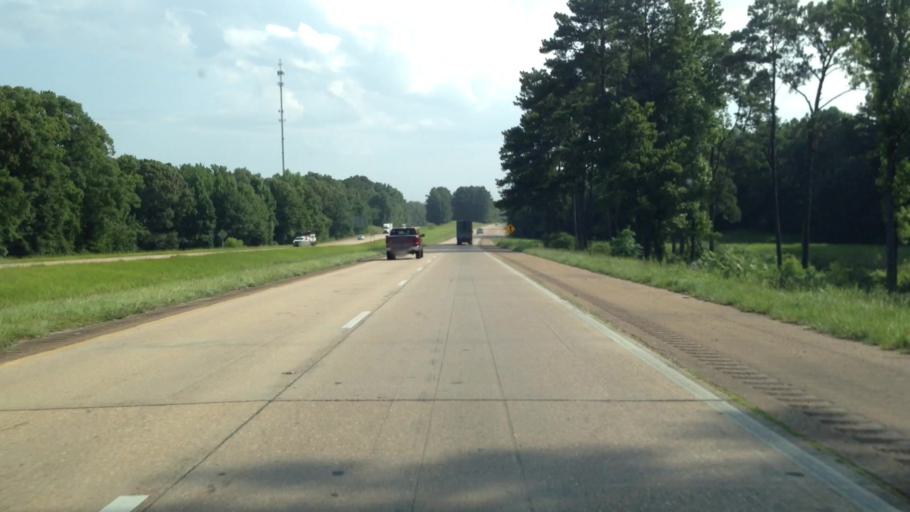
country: US
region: Mississippi
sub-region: Copiah County
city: Crystal Springs
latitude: 32.0154
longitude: -90.3615
